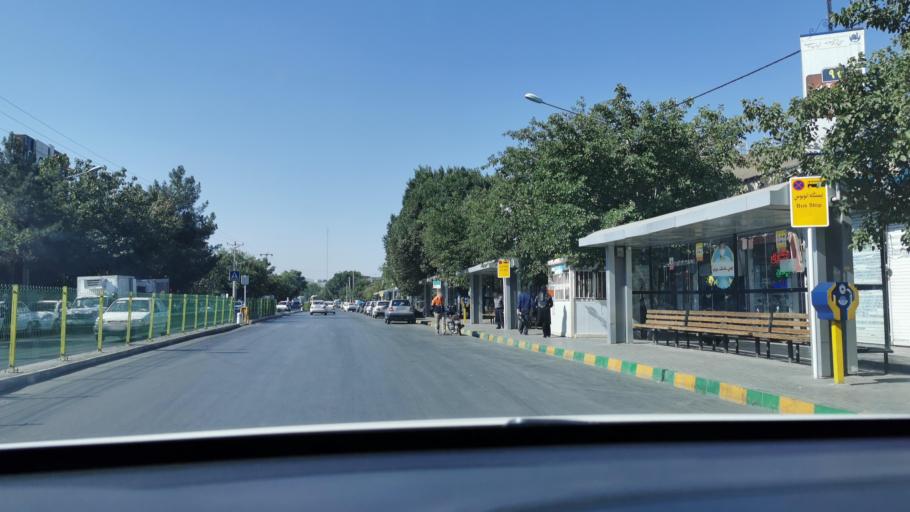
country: IR
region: Razavi Khorasan
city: Mashhad
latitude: 36.3408
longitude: 59.6282
